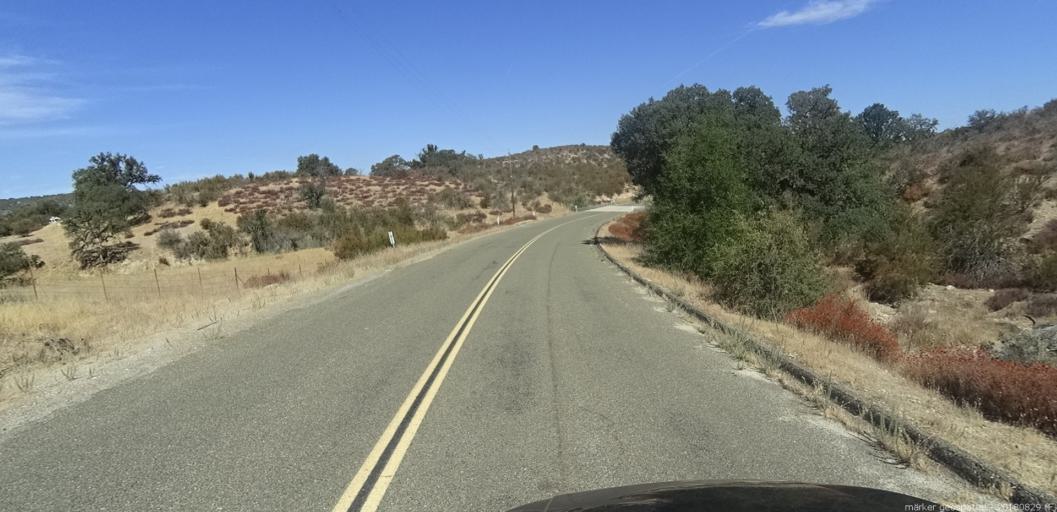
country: US
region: California
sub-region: San Luis Obispo County
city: Lake Nacimiento
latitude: 35.8073
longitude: -120.9812
